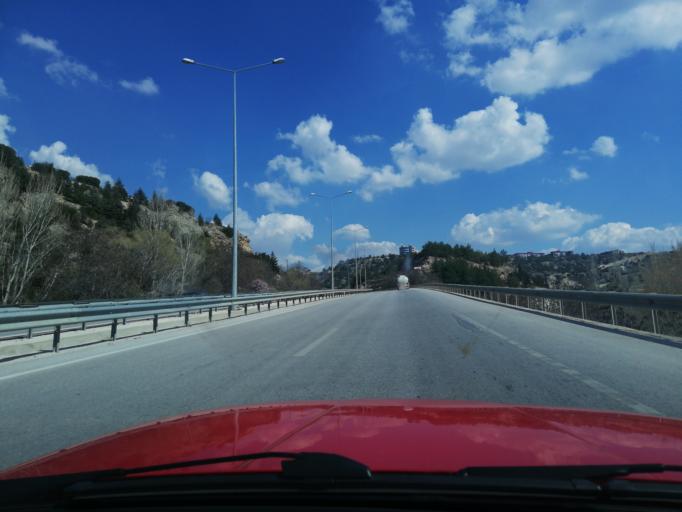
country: TR
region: Burdur
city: Burdur
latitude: 37.6982
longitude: 30.3275
